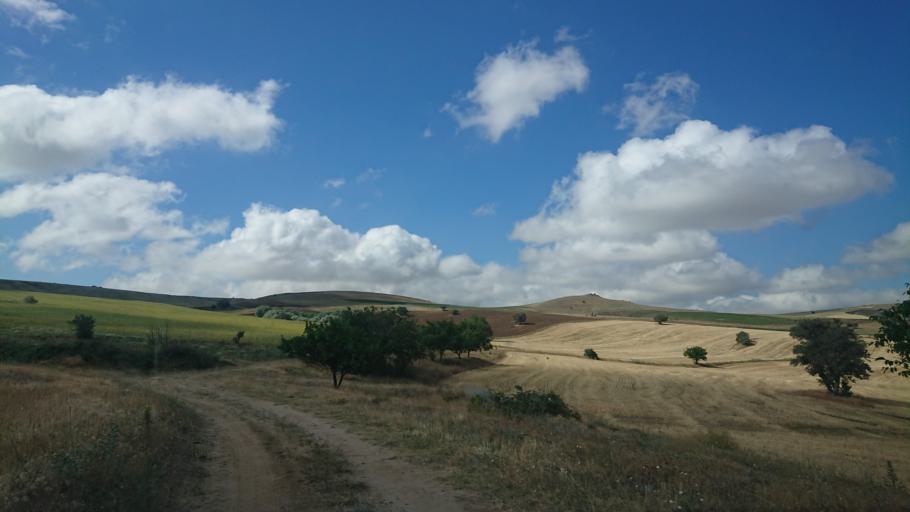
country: TR
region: Aksaray
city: Agacoren
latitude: 38.8454
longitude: 33.9365
